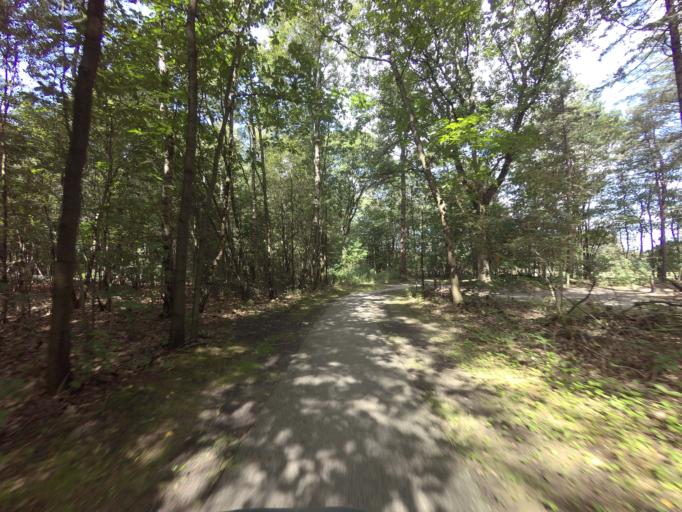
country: NL
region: Overijssel
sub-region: Gemeente Staphorst
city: Staphorst
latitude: 52.6221
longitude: 6.2716
